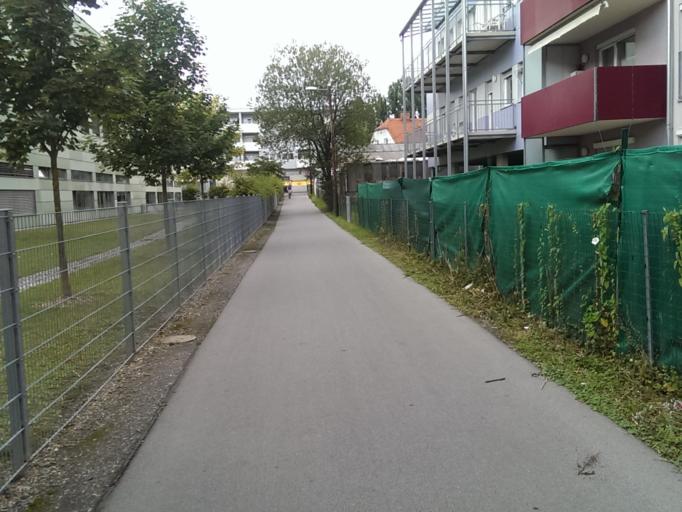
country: AT
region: Styria
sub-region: Graz Stadt
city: Graz
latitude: 47.0592
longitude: 15.4646
